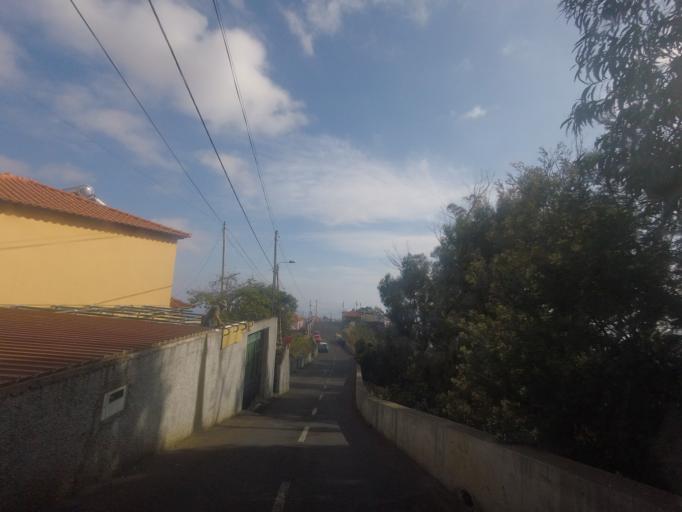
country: PT
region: Madeira
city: Camara de Lobos
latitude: 32.6747
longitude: -16.9540
